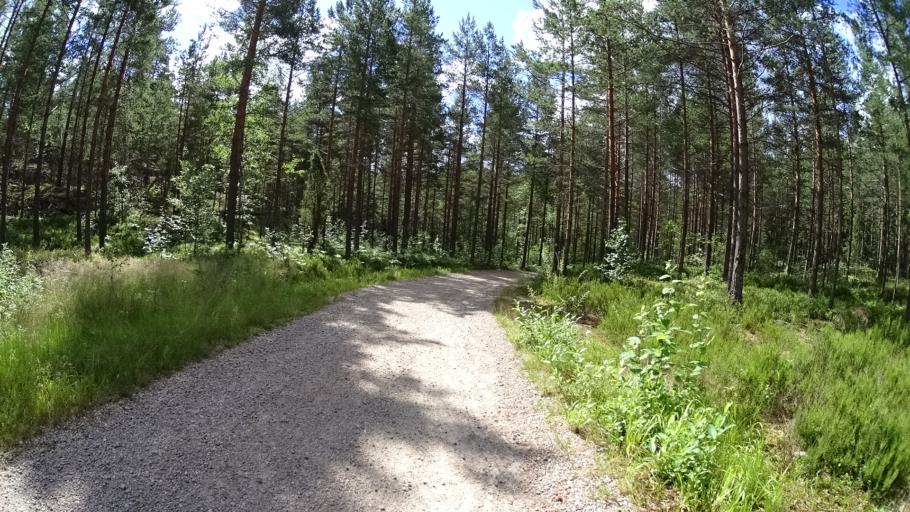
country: FI
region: Uusimaa
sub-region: Helsinki
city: Espoo
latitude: 60.2676
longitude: 24.6272
